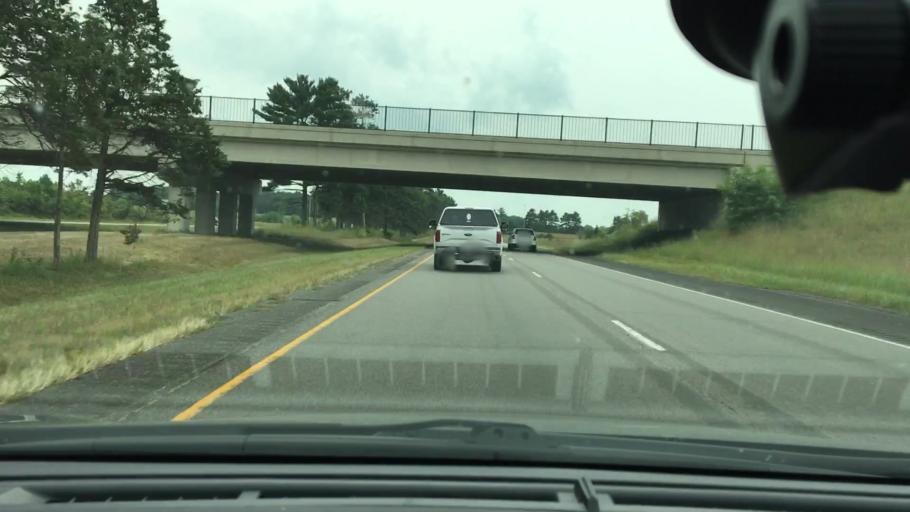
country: US
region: Minnesota
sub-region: Sherburne County
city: Zimmerman
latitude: 45.5022
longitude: -93.5830
